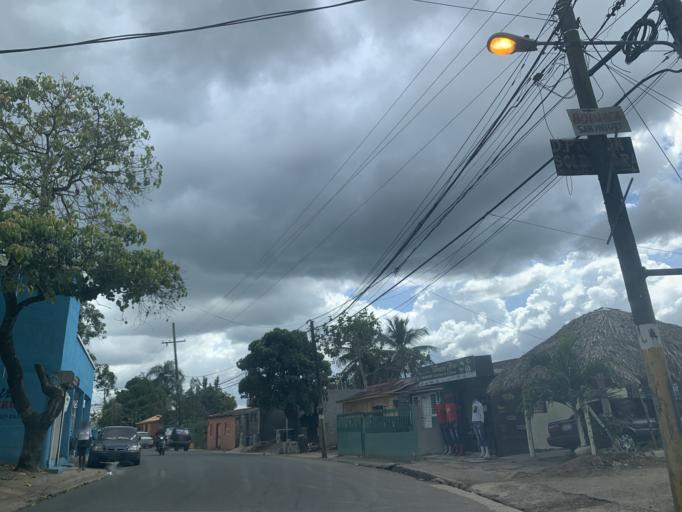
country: DO
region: Monte Plata
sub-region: Yamasa
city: Yamasa
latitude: 18.7770
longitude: -70.0274
